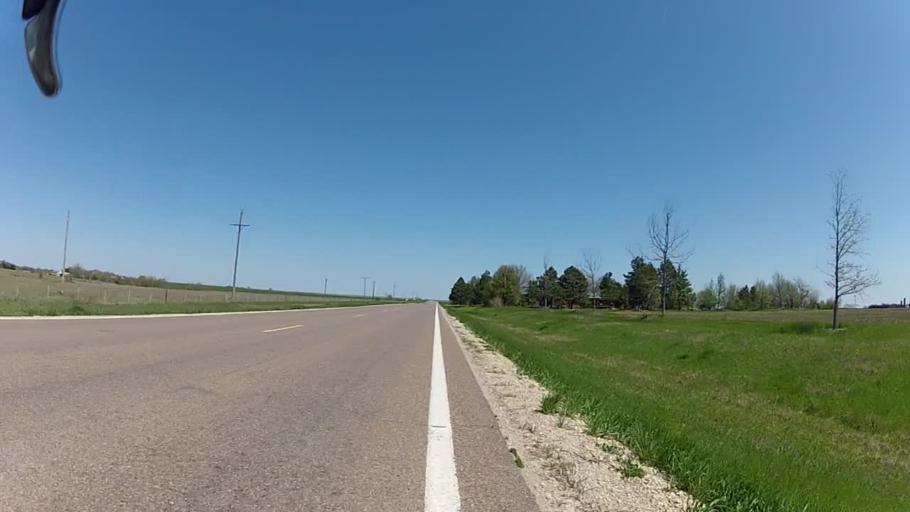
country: US
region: Kansas
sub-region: Riley County
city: Manhattan
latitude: 38.9652
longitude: -96.5200
